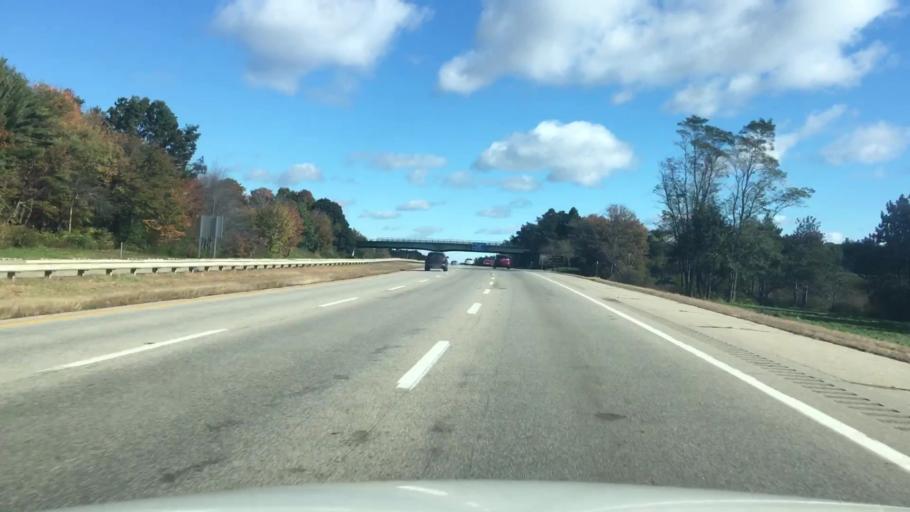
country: US
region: Maine
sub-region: York County
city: Kittery
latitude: 43.1216
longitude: -70.7256
